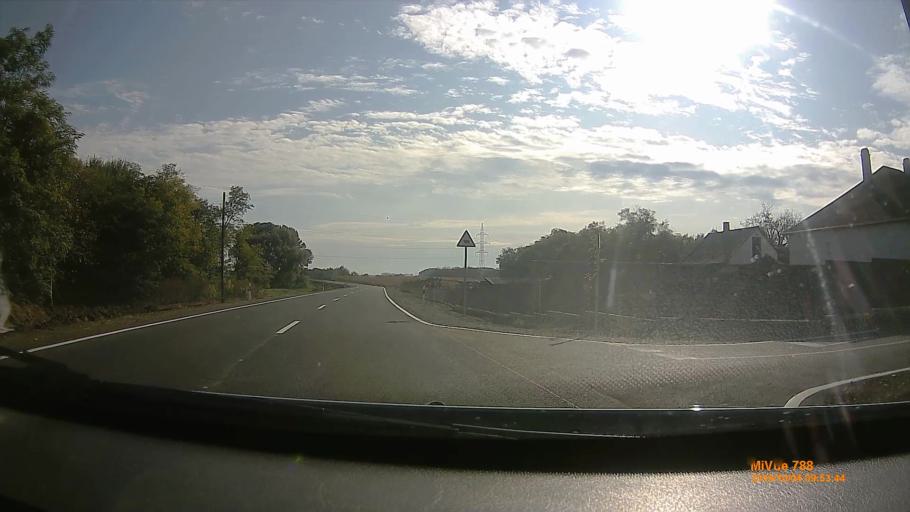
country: HU
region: Szabolcs-Szatmar-Bereg
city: Nyiregyhaza
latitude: 47.9421
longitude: 21.6612
